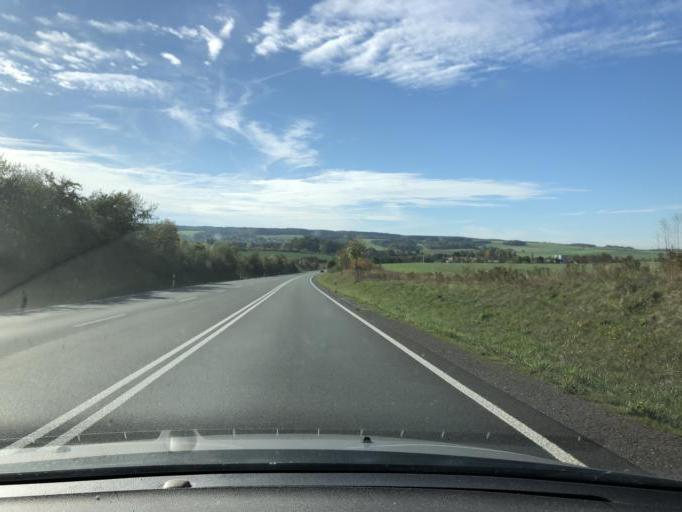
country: DE
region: Thuringia
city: Miesitz
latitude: 50.7447
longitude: 11.8459
